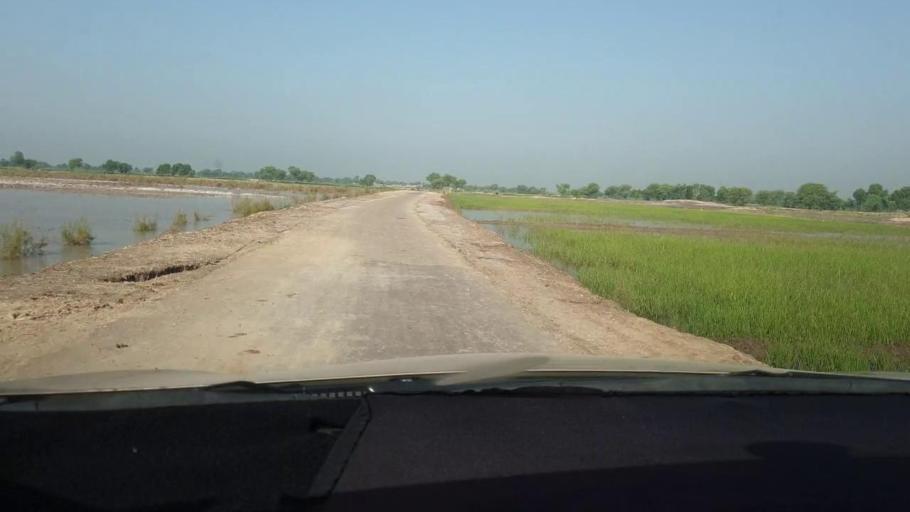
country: PK
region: Sindh
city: Miro Khan
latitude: 27.7531
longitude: 68.1605
